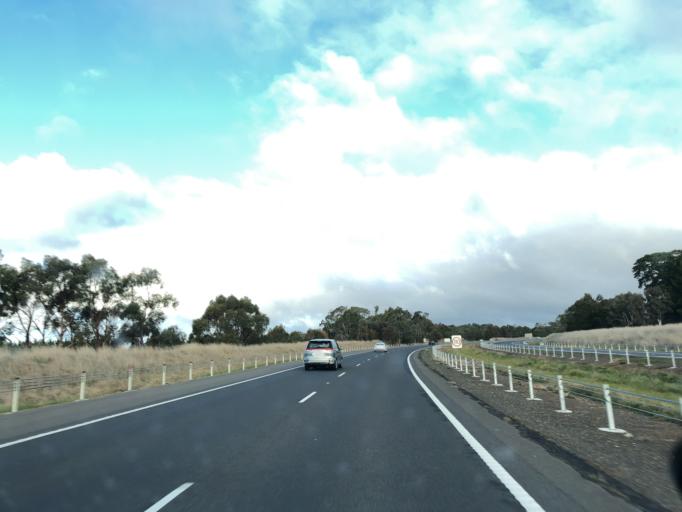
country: AU
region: Victoria
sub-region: Mount Alexander
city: Castlemaine
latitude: -37.2460
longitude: 144.4709
